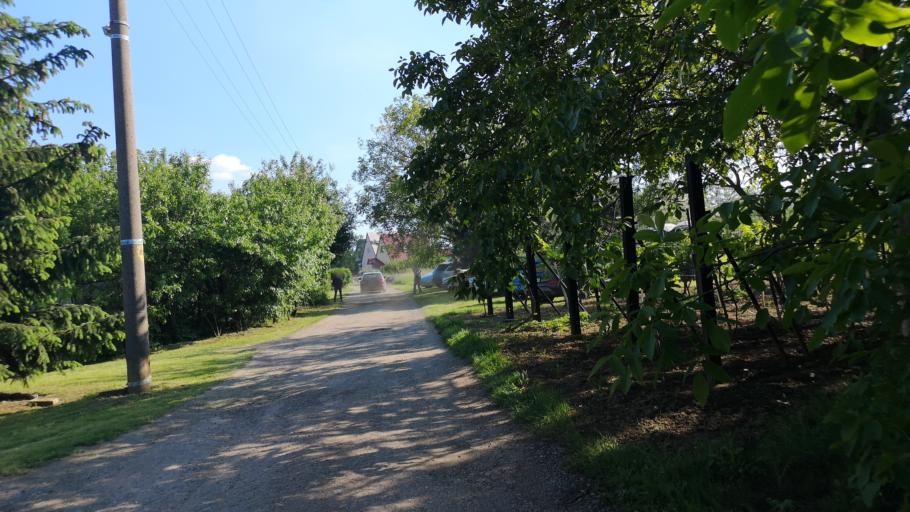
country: SK
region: Nitriansky
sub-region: Okres Nitra
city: Nitra
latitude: 48.2576
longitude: 18.0820
